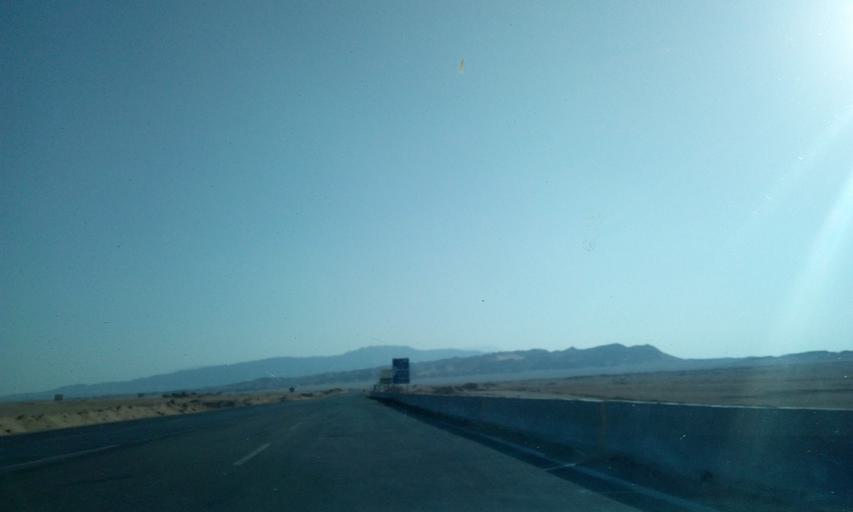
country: EG
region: As Suways
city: Ain Sukhna
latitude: 29.0847
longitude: 32.6332
